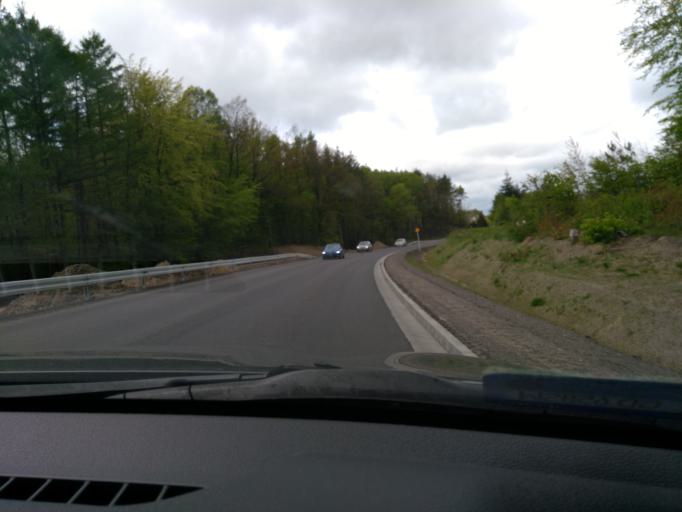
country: PL
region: Pomeranian Voivodeship
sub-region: Powiat kartuski
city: Kartuzy
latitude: 54.3423
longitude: 18.1643
